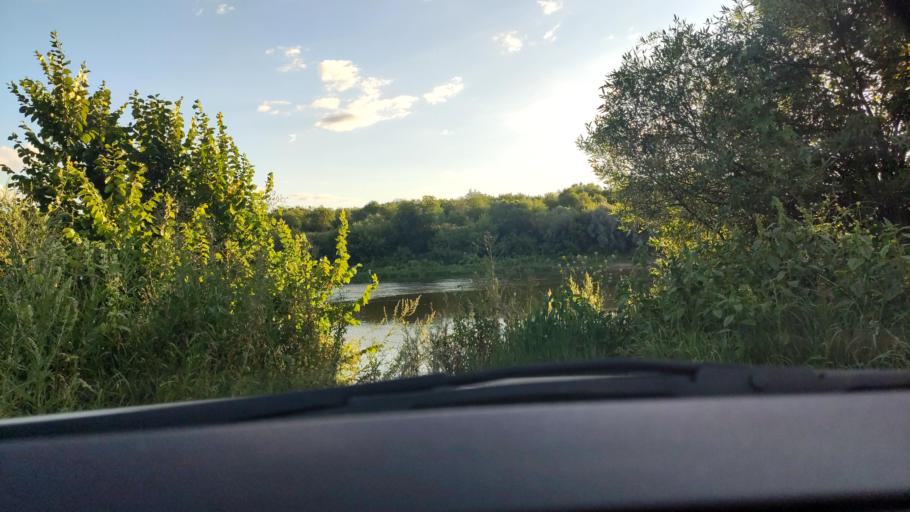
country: RU
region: Voronezj
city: Semiluki
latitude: 51.6816
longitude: 39.0475
